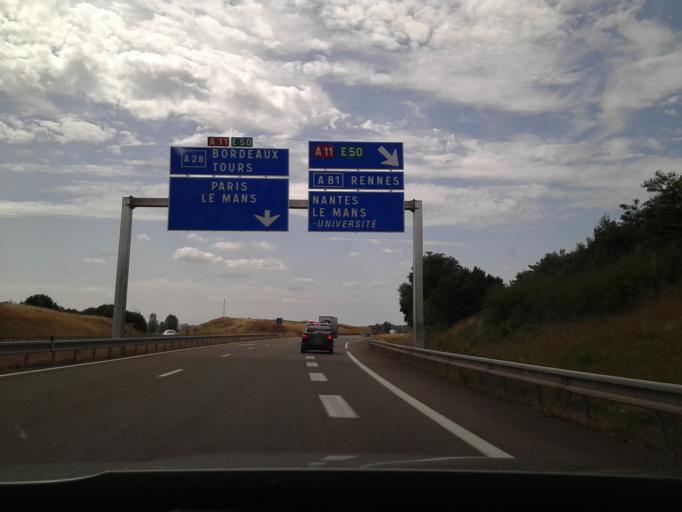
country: FR
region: Pays de la Loire
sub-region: Departement de la Sarthe
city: Saint-Saturnin
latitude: 48.0582
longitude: 0.1760
